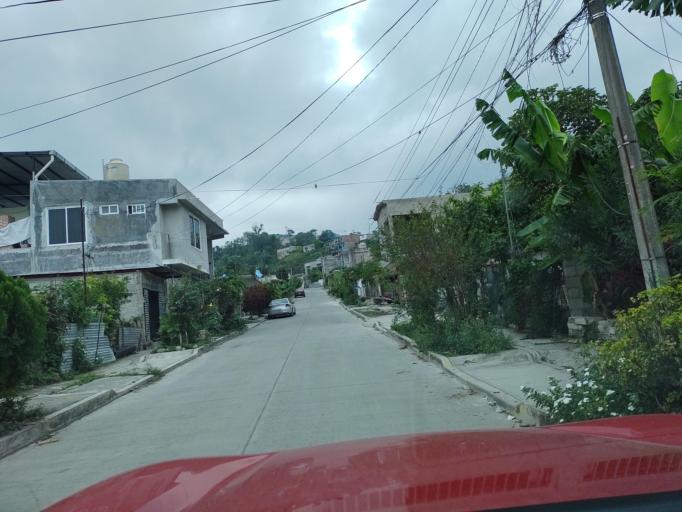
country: MX
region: Veracruz
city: Papantla de Olarte
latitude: 20.4632
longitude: -97.3305
